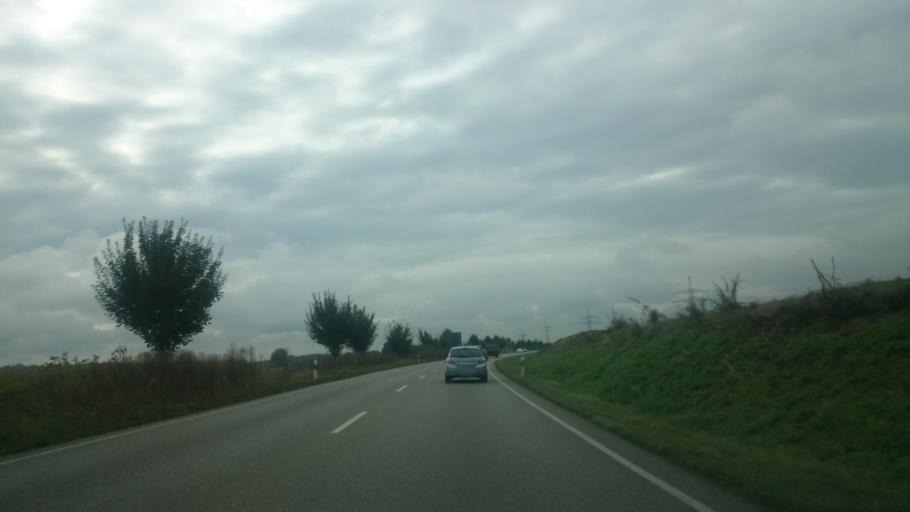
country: DE
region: Bavaria
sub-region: Swabia
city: Friedberg
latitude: 48.3788
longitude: 10.9618
